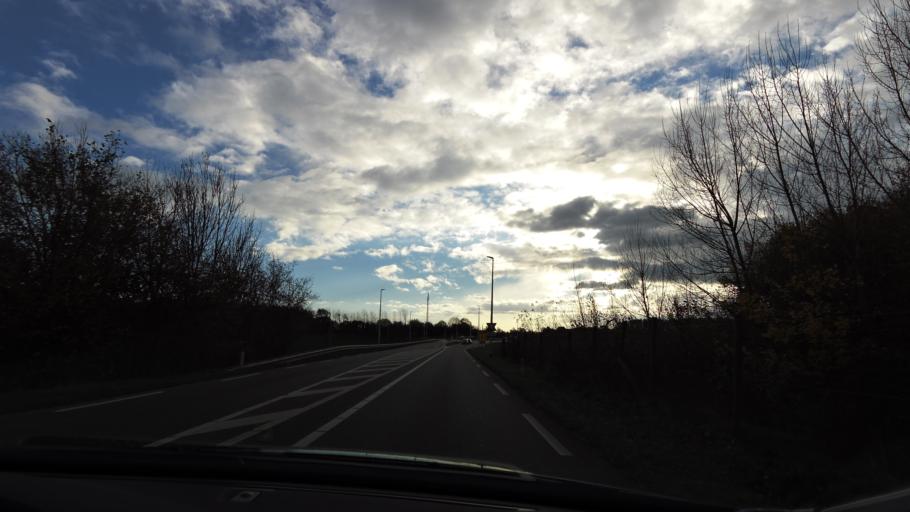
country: NL
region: Limburg
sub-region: Gemeente Onderbanken
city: Merkelbeek
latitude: 50.9476
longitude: 5.9471
